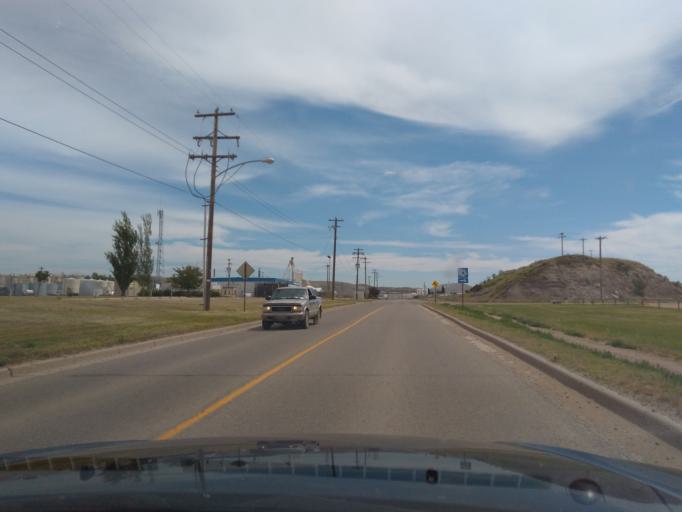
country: CA
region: Alberta
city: Three Hills
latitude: 51.4618
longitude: -112.7258
